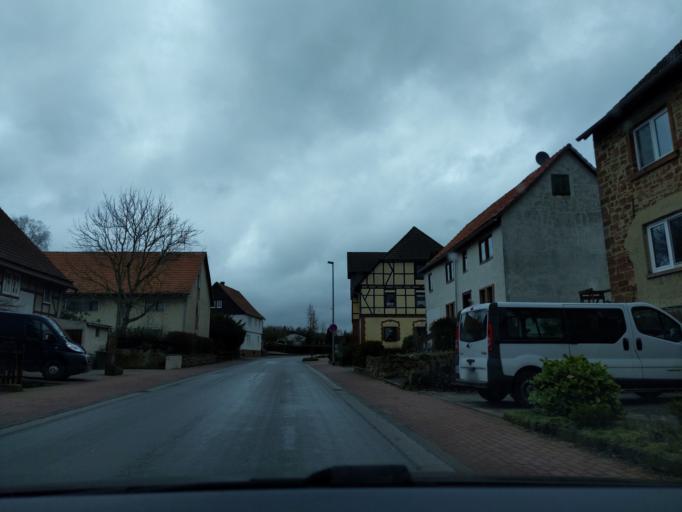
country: DE
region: Hesse
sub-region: Regierungsbezirk Kassel
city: Sachsenhausen
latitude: 51.2741
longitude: 8.9864
